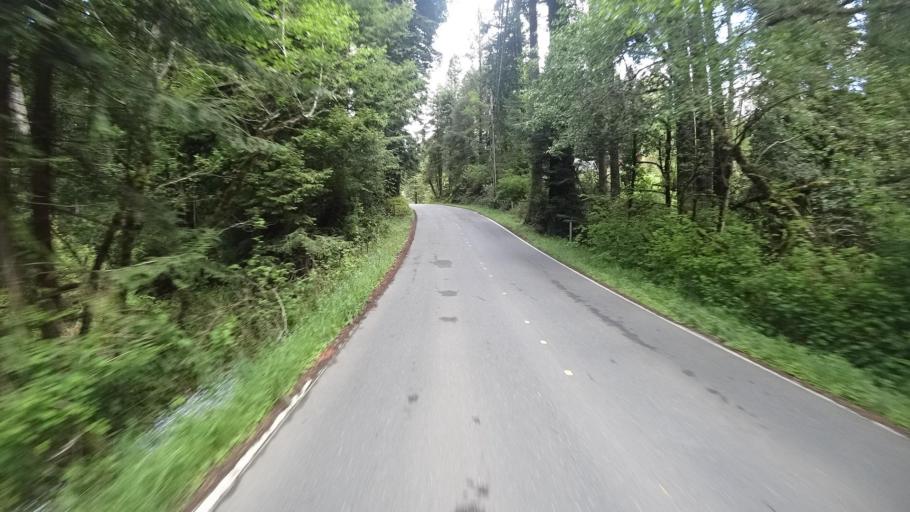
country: US
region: California
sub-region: Humboldt County
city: Blue Lake
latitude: 40.9122
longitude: -124.0232
